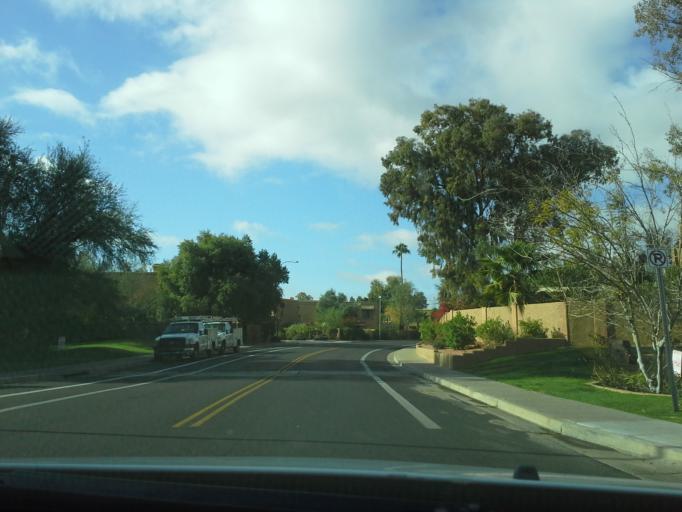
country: US
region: Arizona
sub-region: Maricopa County
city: Paradise Valley
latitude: 33.5820
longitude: -112.0585
